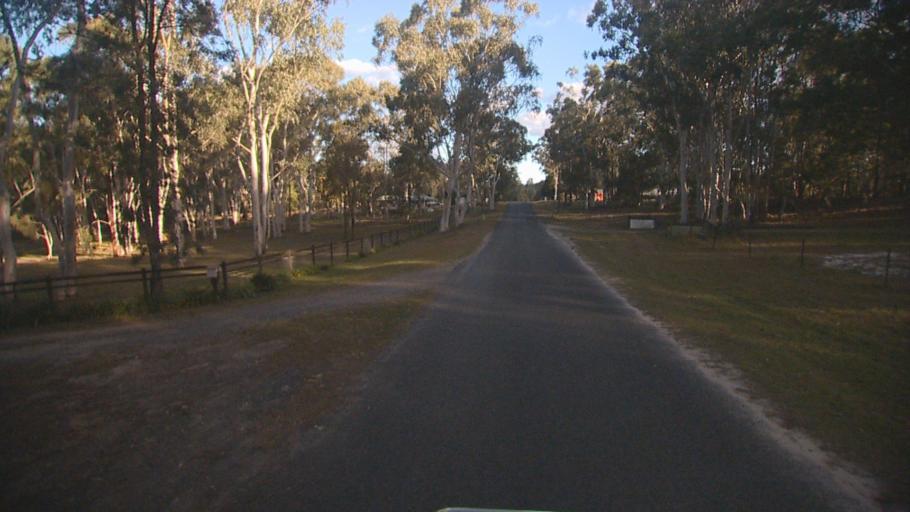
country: AU
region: Queensland
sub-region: Logan
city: Cedar Vale
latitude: -27.8460
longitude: 153.1105
